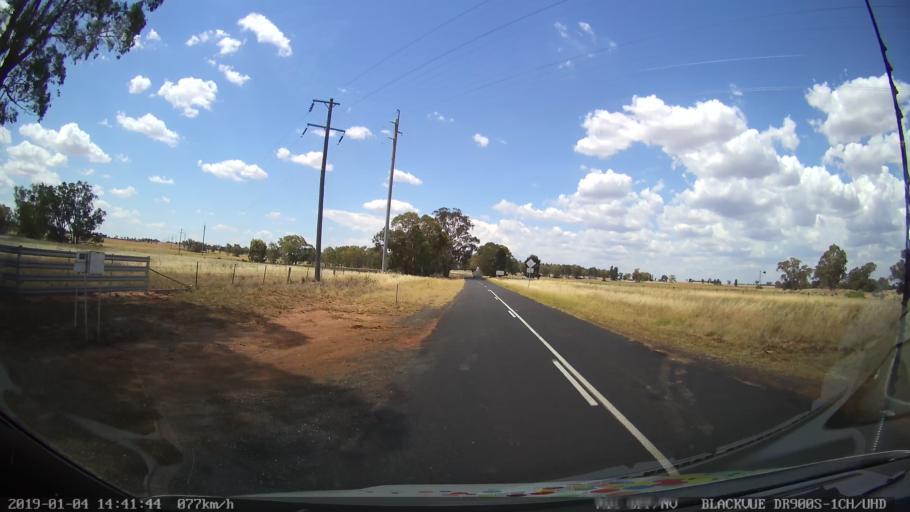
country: AU
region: New South Wales
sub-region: Dubbo Municipality
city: Dubbo
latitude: -32.1358
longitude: 148.6377
